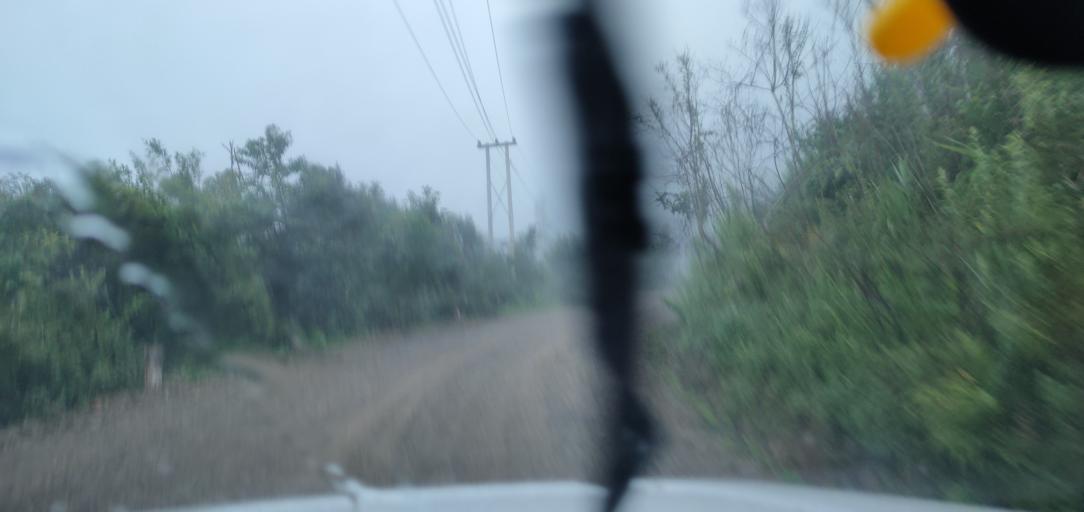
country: LA
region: Phongsali
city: Phongsali
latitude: 21.3980
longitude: 102.1923
